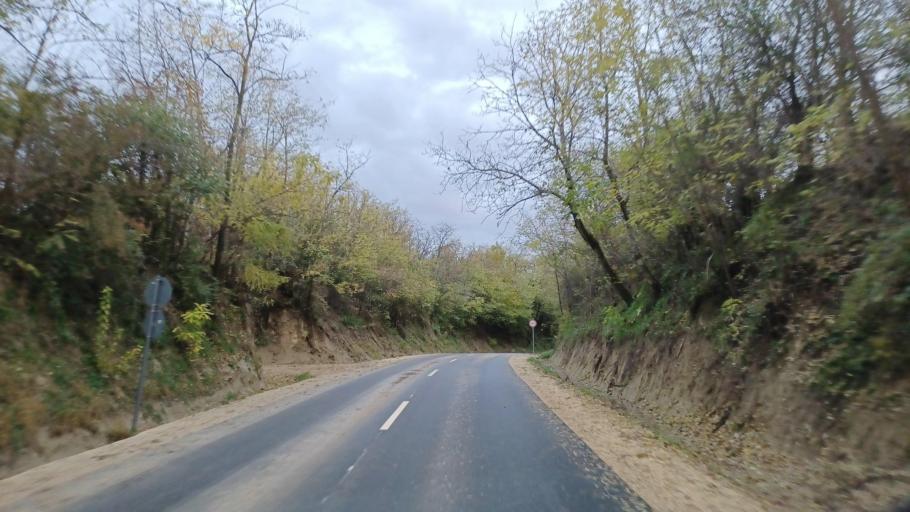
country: HU
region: Tolna
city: Gyonk
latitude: 46.5739
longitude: 18.4588
